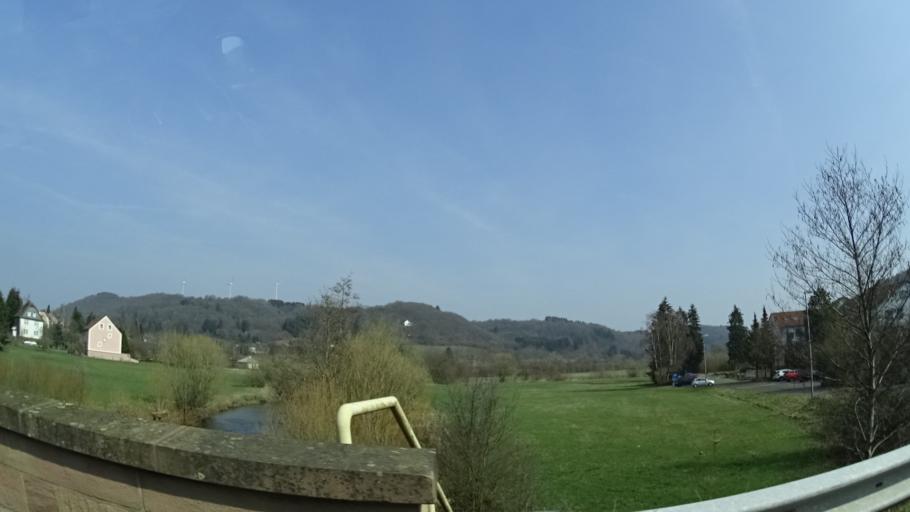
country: DE
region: Rheinland-Pfalz
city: Hoppstadten-Weiersbach
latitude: 49.6128
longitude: 7.1952
